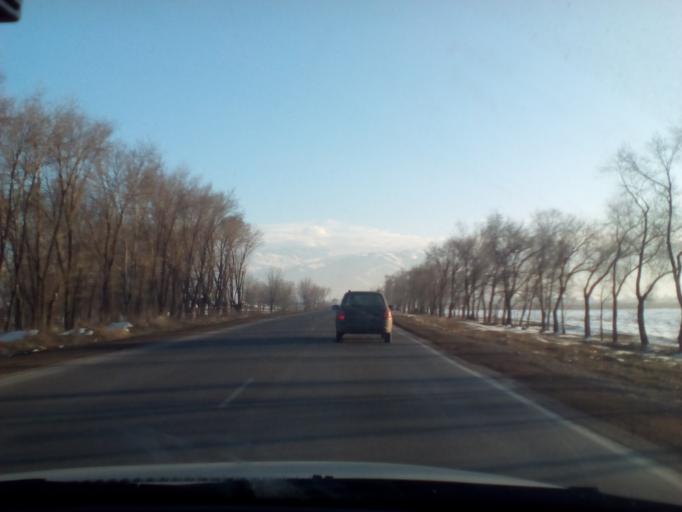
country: KZ
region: Almaty Oblysy
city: Burunday
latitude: 43.2138
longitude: 76.4147
